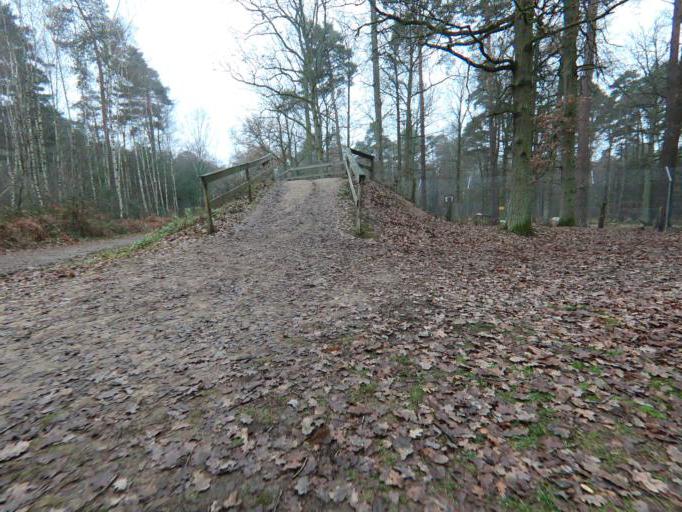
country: DE
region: Hesse
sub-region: Regierungsbezirk Darmstadt
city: Hanau am Main
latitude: 50.0785
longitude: 8.9089
